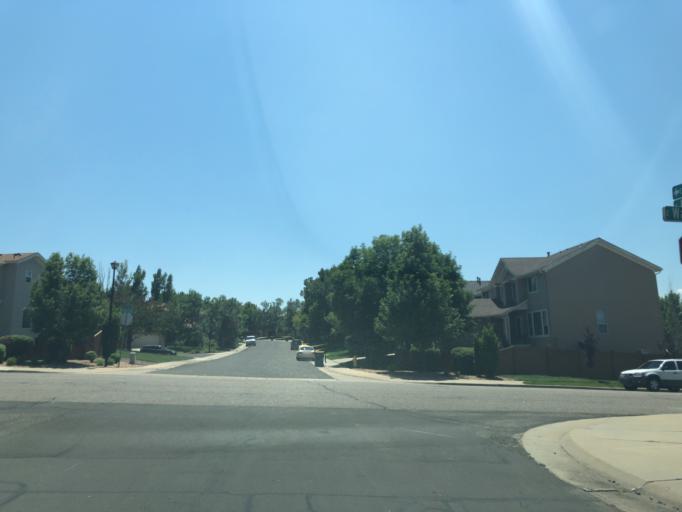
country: US
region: Colorado
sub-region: Arapahoe County
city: Dove Valley
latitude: 39.6306
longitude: -104.7688
